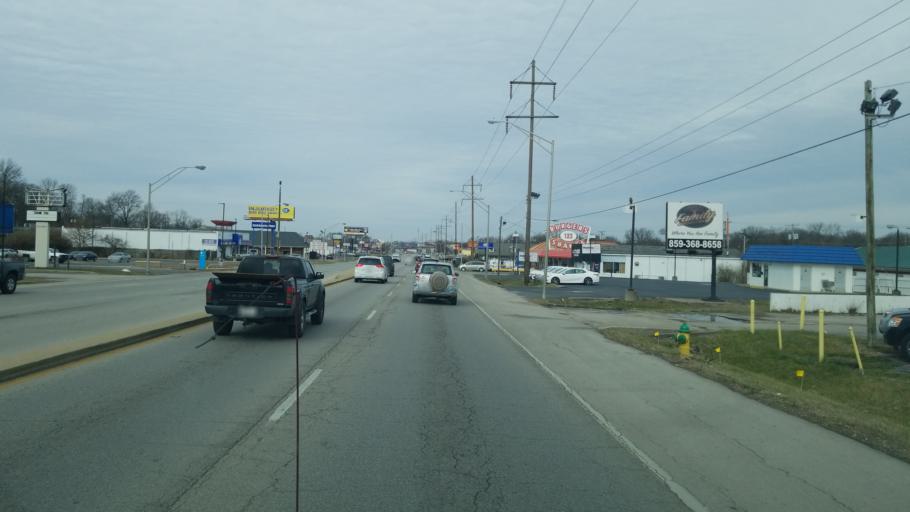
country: US
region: Kentucky
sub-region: Fayette County
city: Lexington-Fayette
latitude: 38.0611
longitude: -84.4658
